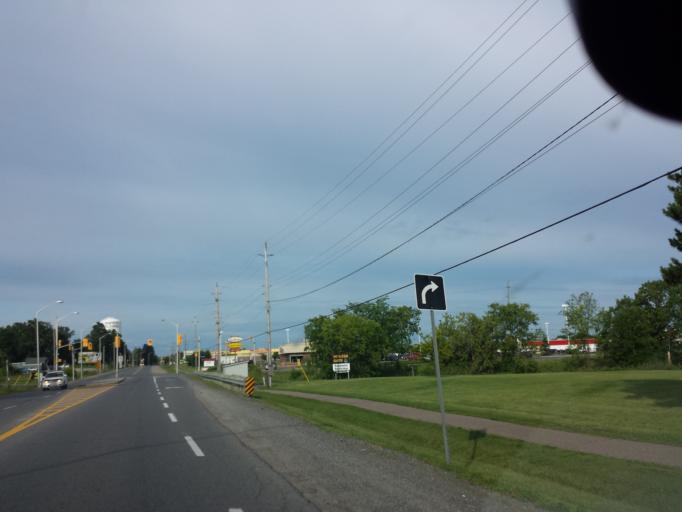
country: CA
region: Ontario
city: Renfrew
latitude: 45.4766
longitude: -76.6571
